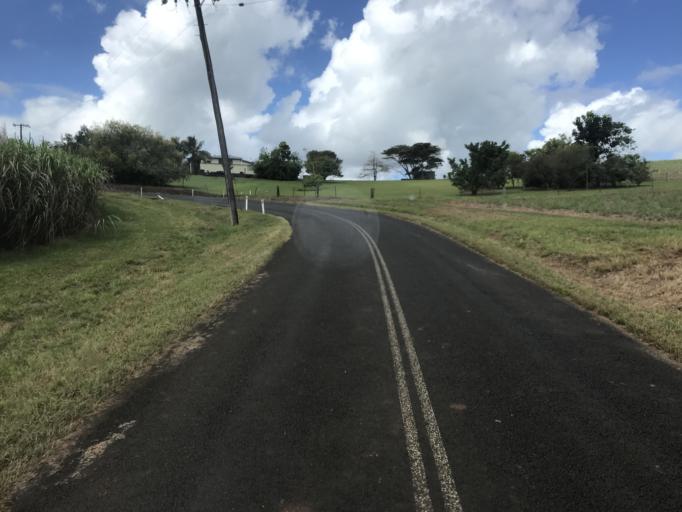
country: AU
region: Queensland
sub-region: Cassowary Coast
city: Innisfail
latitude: -17.5540
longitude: 145.8891
